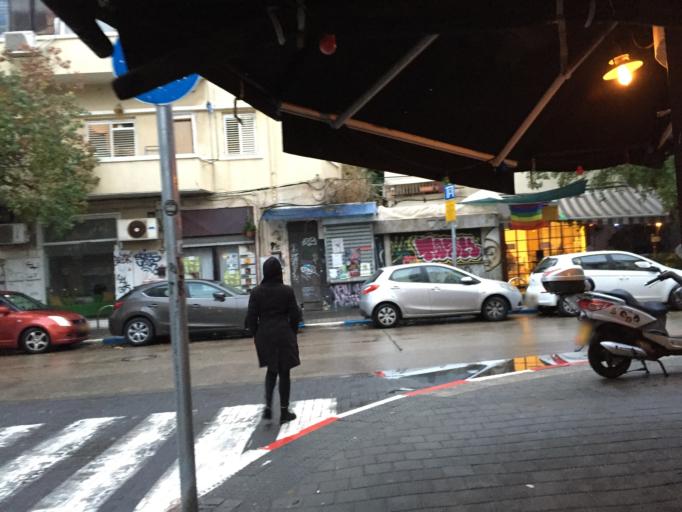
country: IL
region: Tel Aviv
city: Yafo
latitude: 32.0571
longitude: 34.7695
